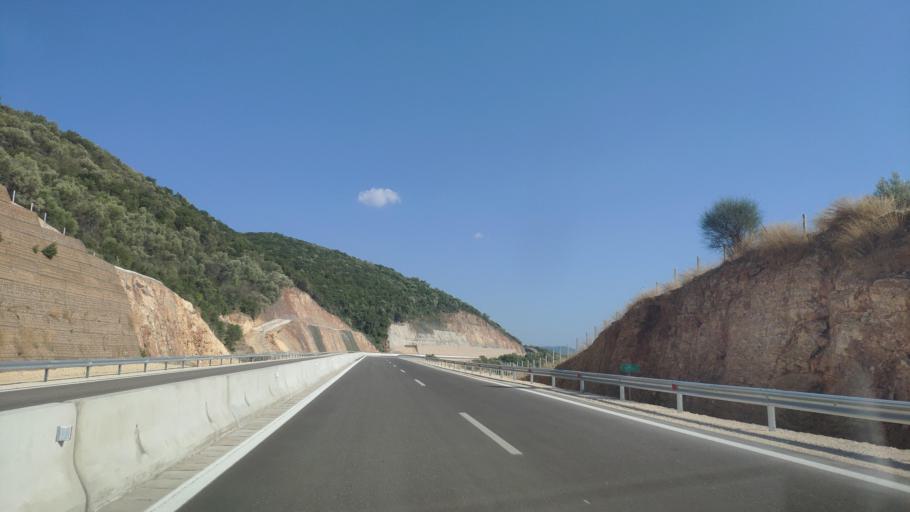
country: GR
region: West Greece
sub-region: Nomos Aitolias kai Akarnanias
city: Stanos
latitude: 38.7779
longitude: 21.1519
